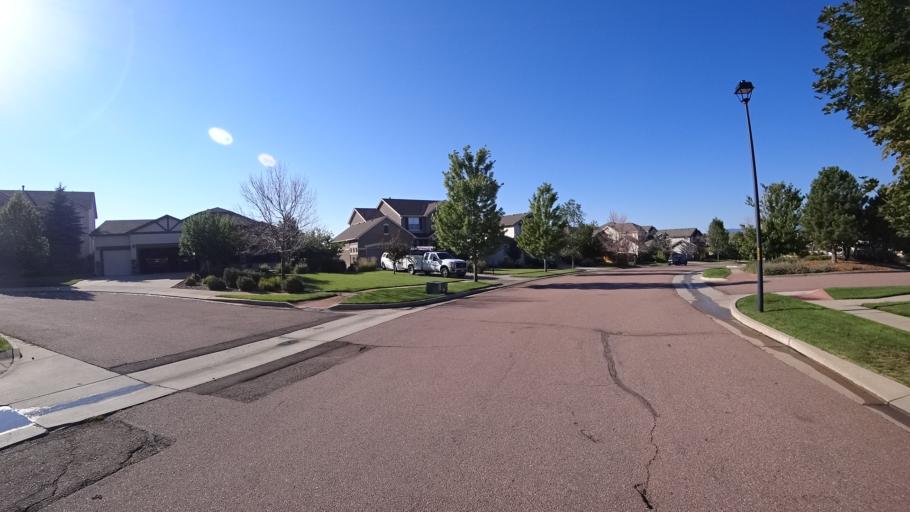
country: US
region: Colorado
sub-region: El Paso County
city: Black Forest
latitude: 38.9761
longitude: -104.7554
